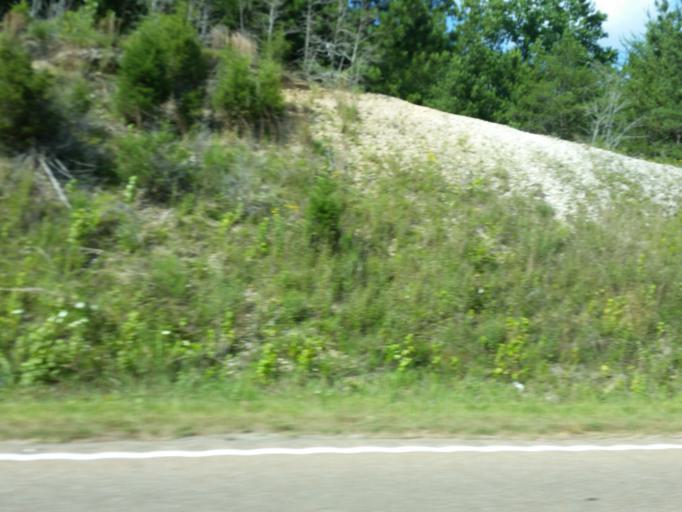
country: US
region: Tennessee
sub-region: Decatur County
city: Parsons
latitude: 35.6369
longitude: -88.0759
